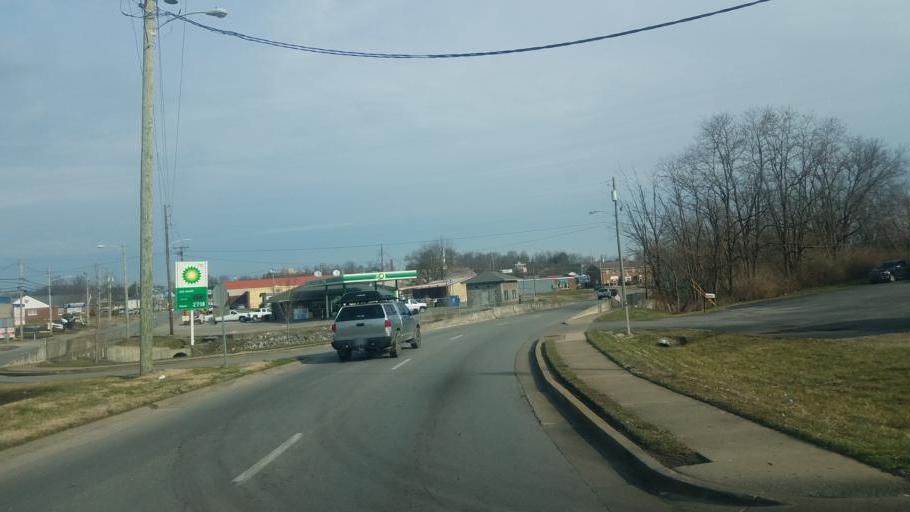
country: US
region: Kentucky
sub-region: Boyle County
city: Danville
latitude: 37.6356
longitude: -84.7749
